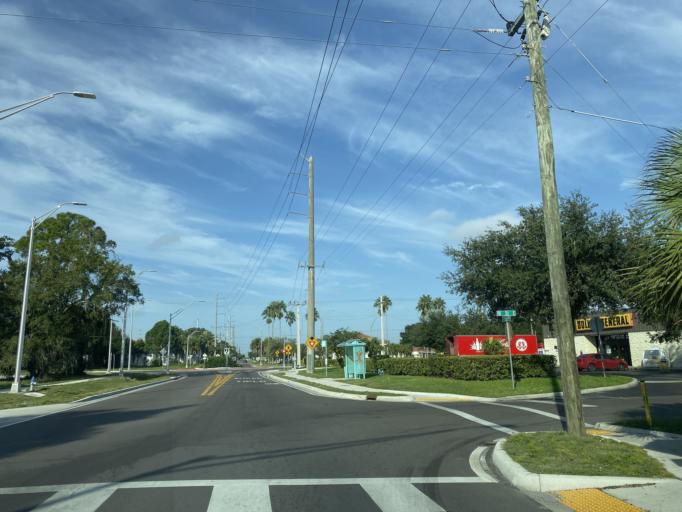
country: US
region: Florida
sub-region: Manatee County
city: Samoset
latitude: 27.4916
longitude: -82.5456
